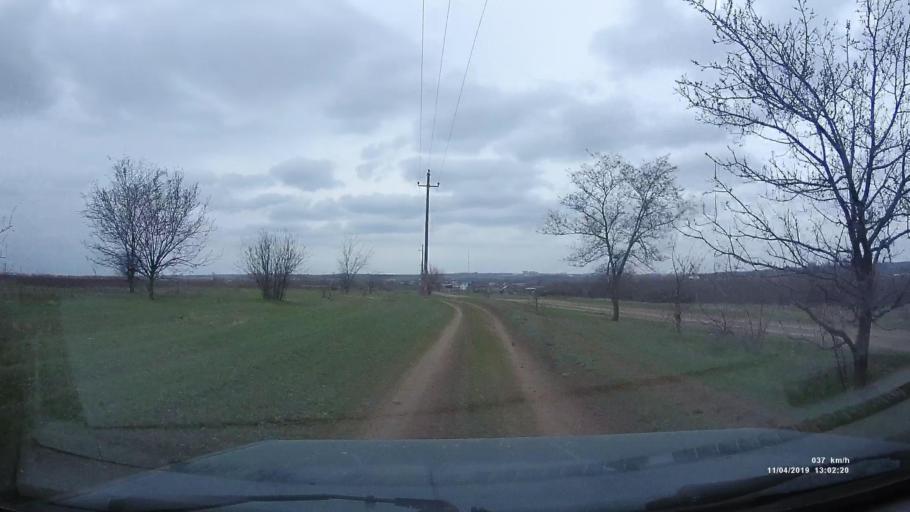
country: RU
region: Rostov
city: Staraya Stanitsa
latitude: 48.2878
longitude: 40.3590
